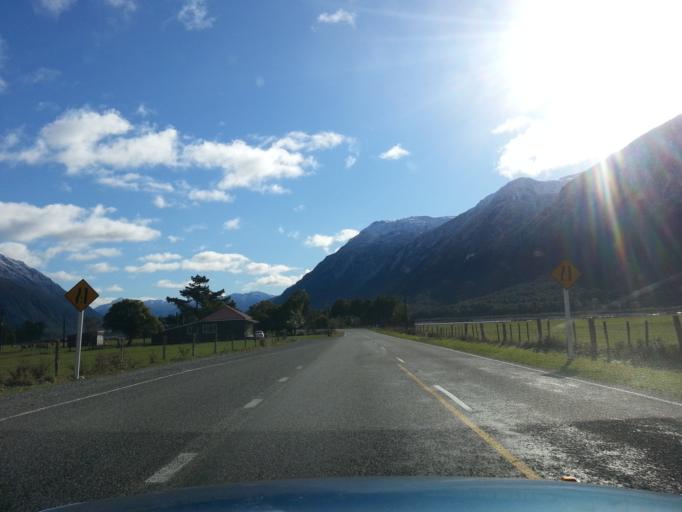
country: NZ
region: West Coast
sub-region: Grey District
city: Greymouth
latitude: -42.7630
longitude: 171.6135
